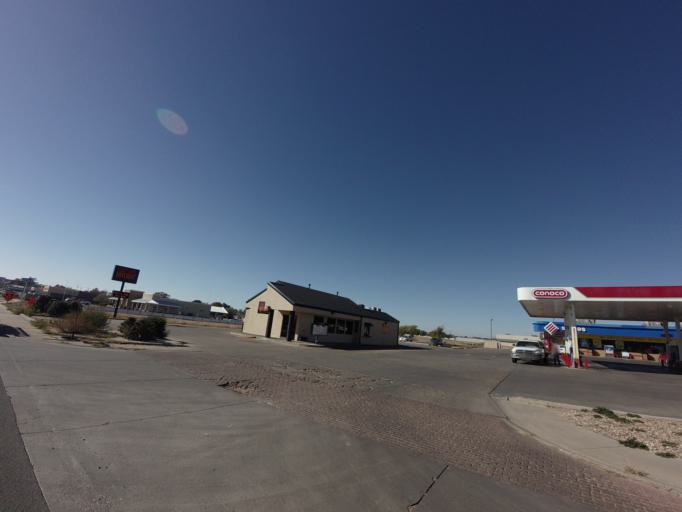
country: US
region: New Mexico
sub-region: Curry County
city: Clovis
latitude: 34.4333
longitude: -103.1966
